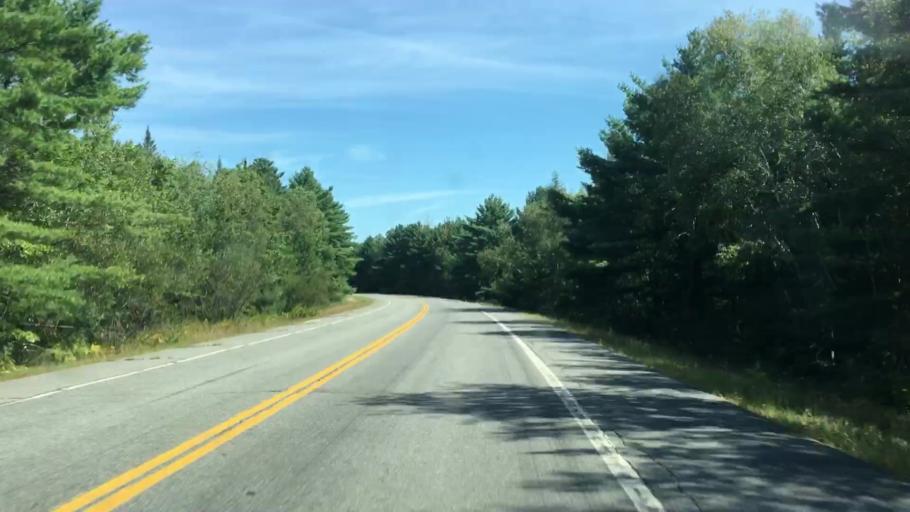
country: US
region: Maine
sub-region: Piscataquis County
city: Milo
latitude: 45.2293
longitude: -68.9502
